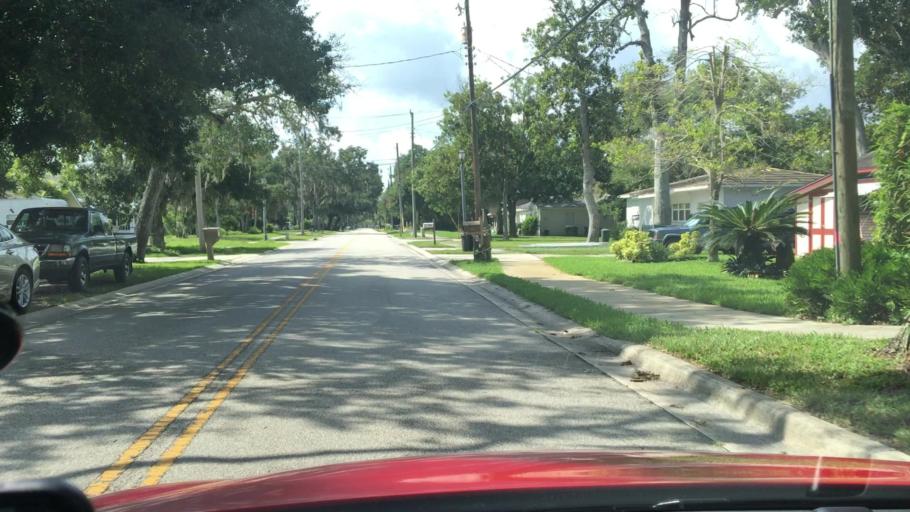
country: US
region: Florida
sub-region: Volusia County
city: Ormond Beach
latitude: 29.2808
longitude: -81.0570
